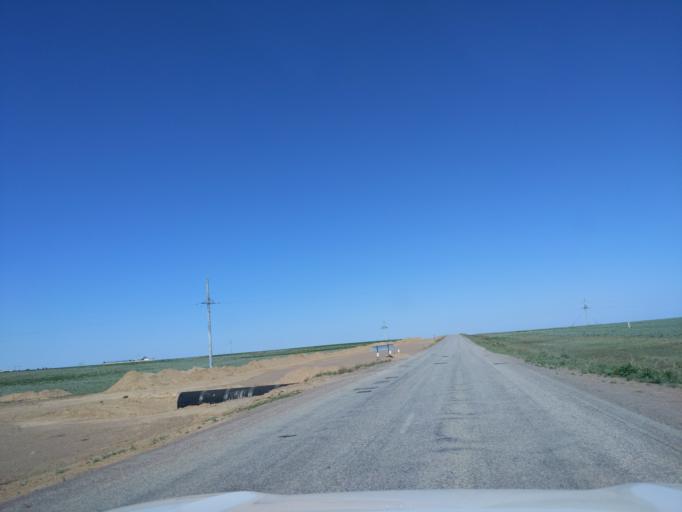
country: KZ
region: Almaty Oblysy
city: Bakanas
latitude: 44.1834
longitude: 75.7964
